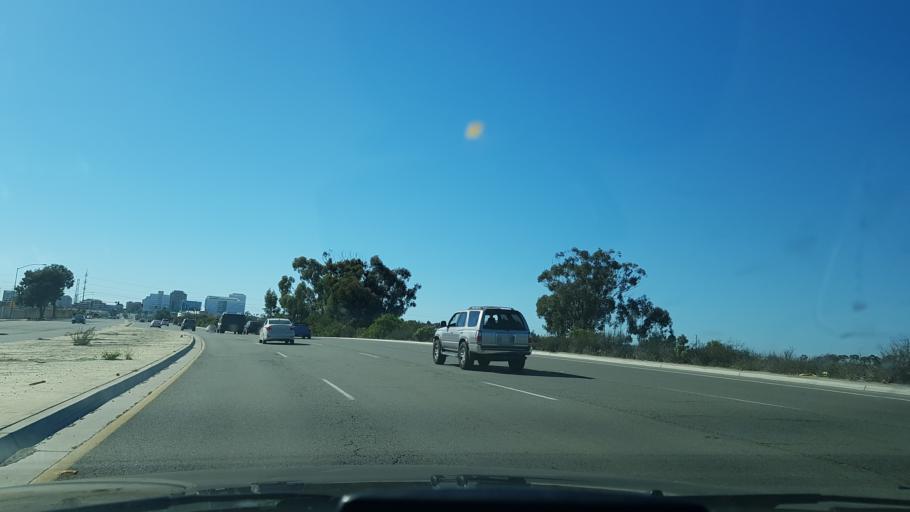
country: US
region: California
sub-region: San Diego County
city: La Jolla
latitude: 32.8769
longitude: -117.1876
